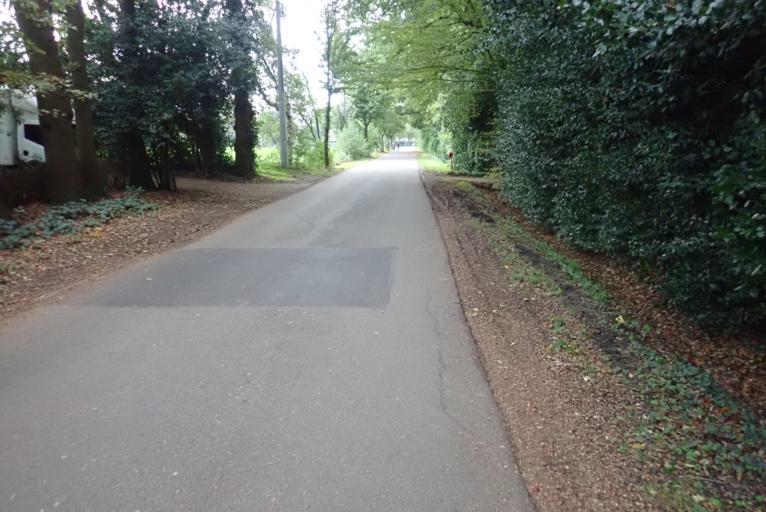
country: BE
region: Flanders
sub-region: Provincie Antwerpen
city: Kalmthout
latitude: 51.3994
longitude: 4.4767
